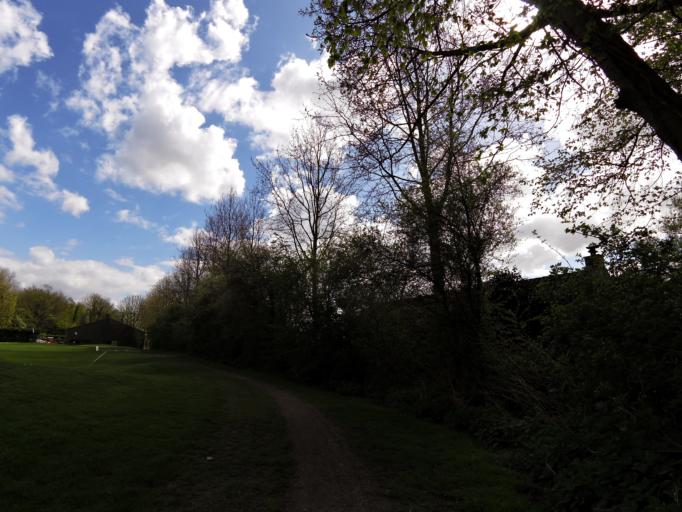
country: NL
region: South Holland
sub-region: Gemeente Binnenmaas
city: Heinenoord
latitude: 51.8346
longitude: 4.4577
